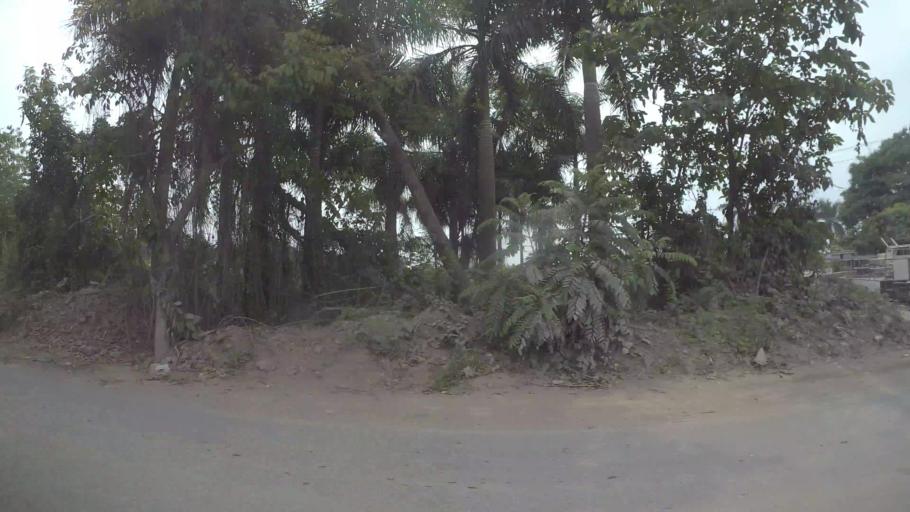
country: VN
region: Ha Noi
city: Cau Dien
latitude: 21.0374
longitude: 105.7380
